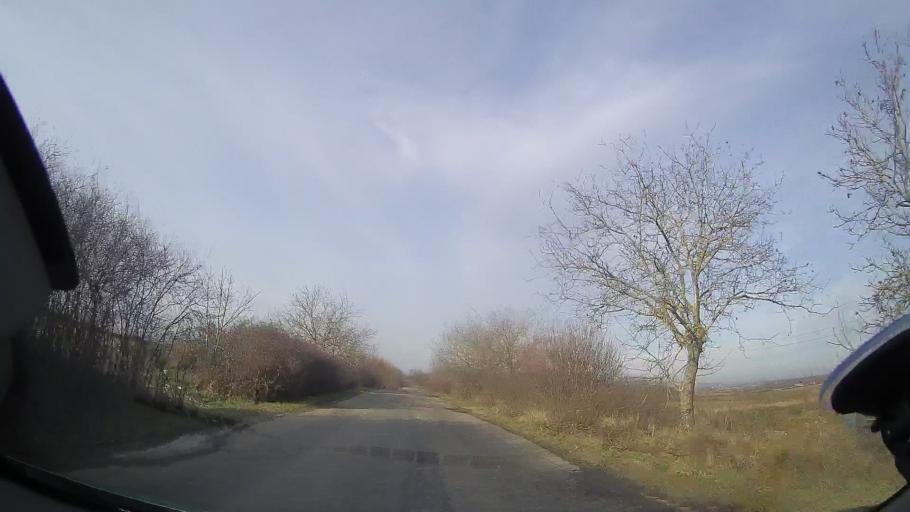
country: RO
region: Bihor
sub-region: Comuna Spinus
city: Spinus
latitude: 47.2103
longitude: 22.1793
